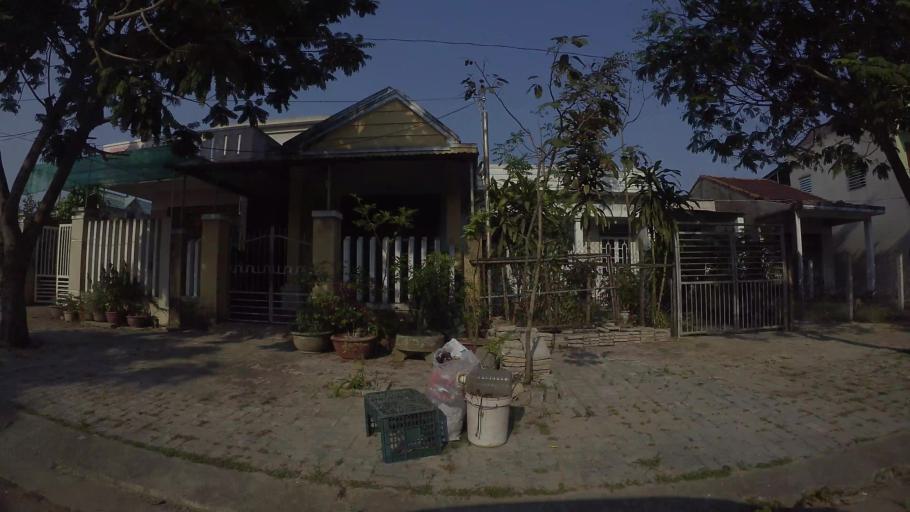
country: VN
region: Da Nang
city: Ngu Hanh Son
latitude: 15.9538
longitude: 108.2575
